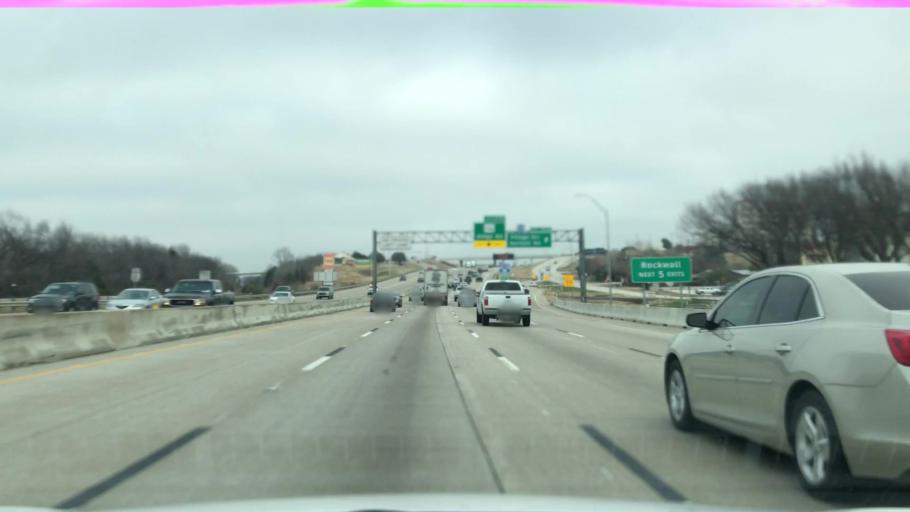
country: US
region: Texas
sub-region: Rockwall County
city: Rockwall
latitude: 32.8932
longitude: -96.4824
